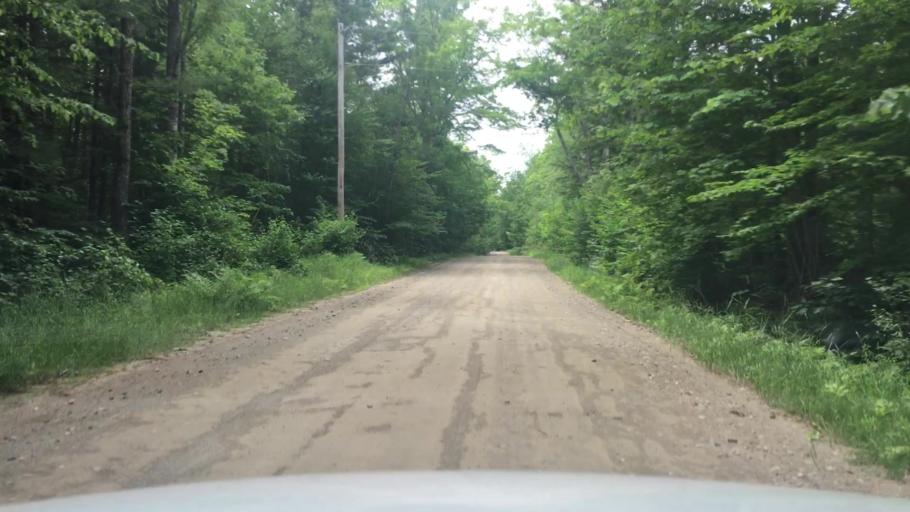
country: US
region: Maine
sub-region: Waldo County
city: Searsmont
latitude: 44.4186
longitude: -69.2611
